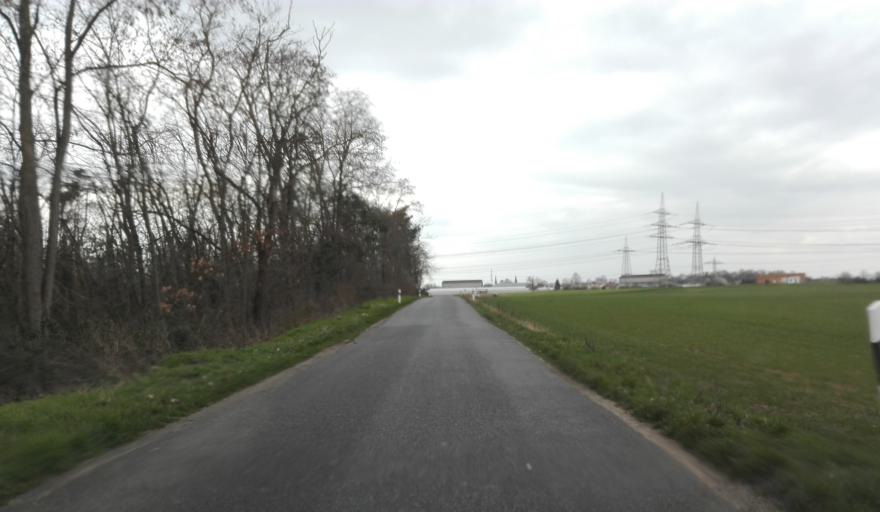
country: DE
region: Baden-Wuerttemberg
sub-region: Karlsruhe Region
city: Plankstadt
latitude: 49.4233
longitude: 8.5784
